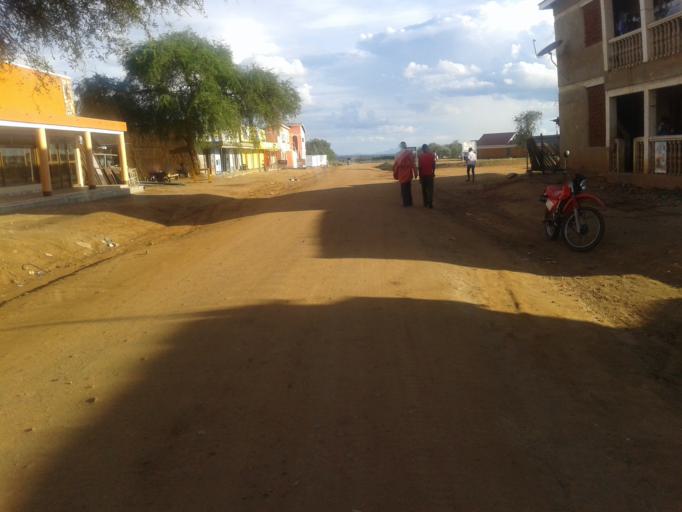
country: UG
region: Northern Region
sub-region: Kotido District
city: Kotido
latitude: 3.0050
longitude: 34.1141
